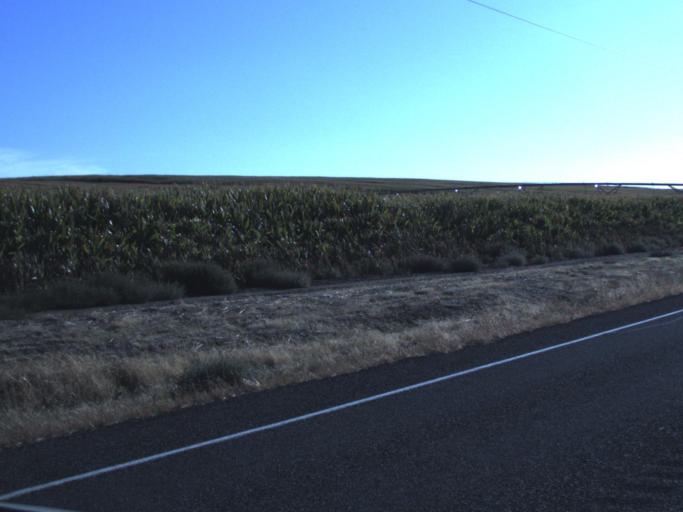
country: US
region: Washington
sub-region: Walla Walla County
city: Burbank
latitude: 46.2618
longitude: -118.7885
